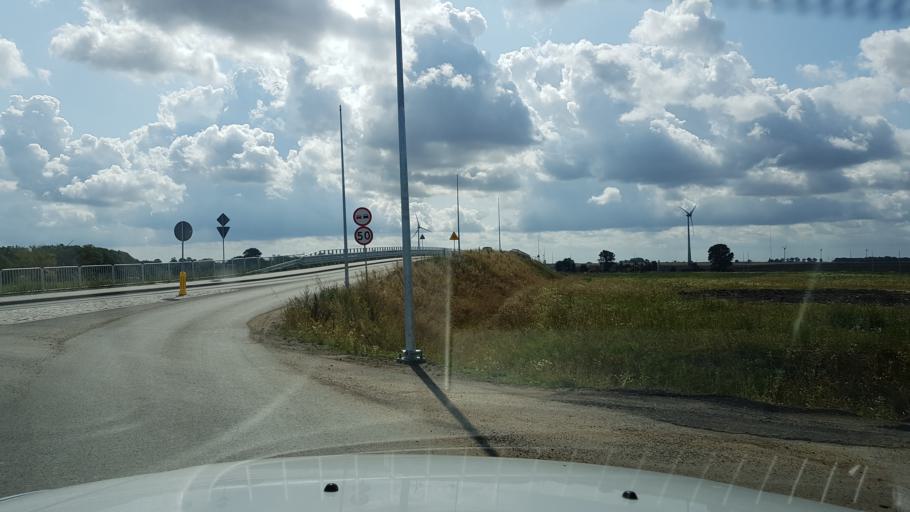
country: PL
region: West Pomeranian Voivodeship
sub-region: Powiat kolobrzeski
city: Ustronie Morskie
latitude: 54.1727
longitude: 15.7475
